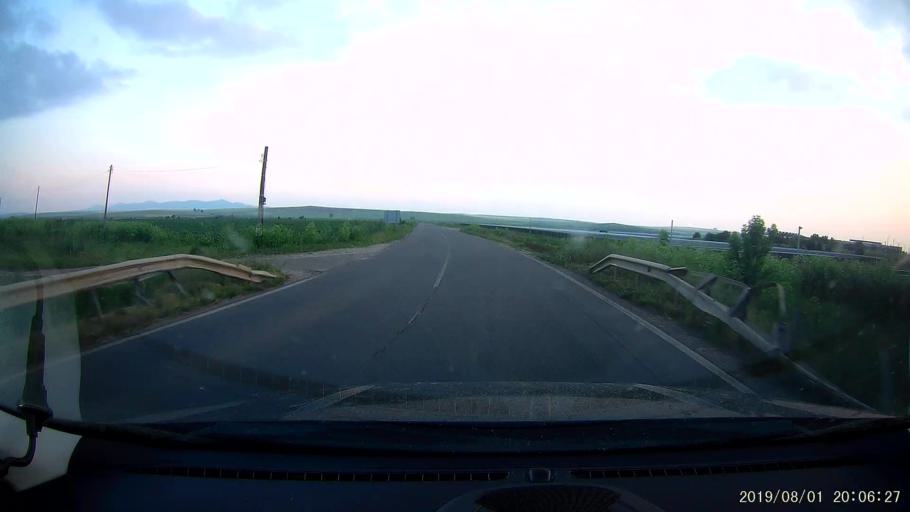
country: BG
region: Yambol
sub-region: Obshtina Yambol
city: Yambol
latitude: 42.5350
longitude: 26.5562
